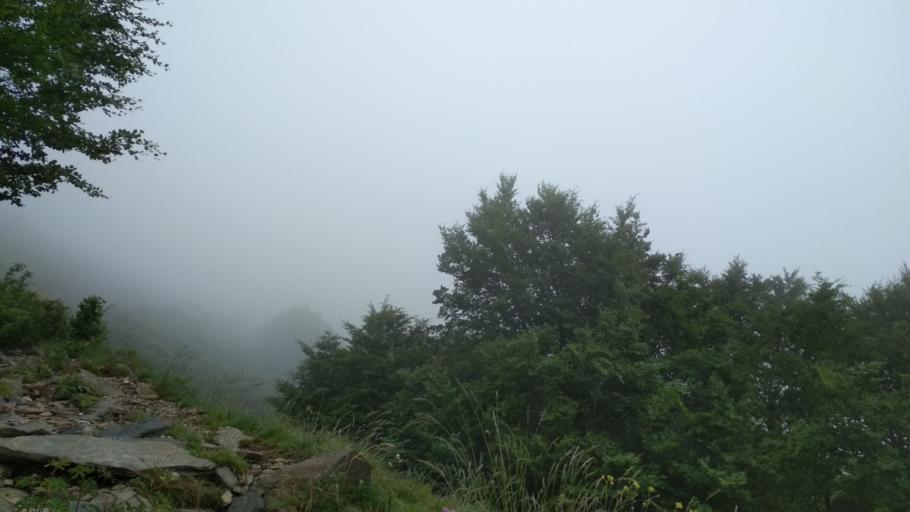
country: ES
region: Catalonia
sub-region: Provincia de Barcelona
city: Fogars de Montclus
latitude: 41.7752
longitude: 2.4390
